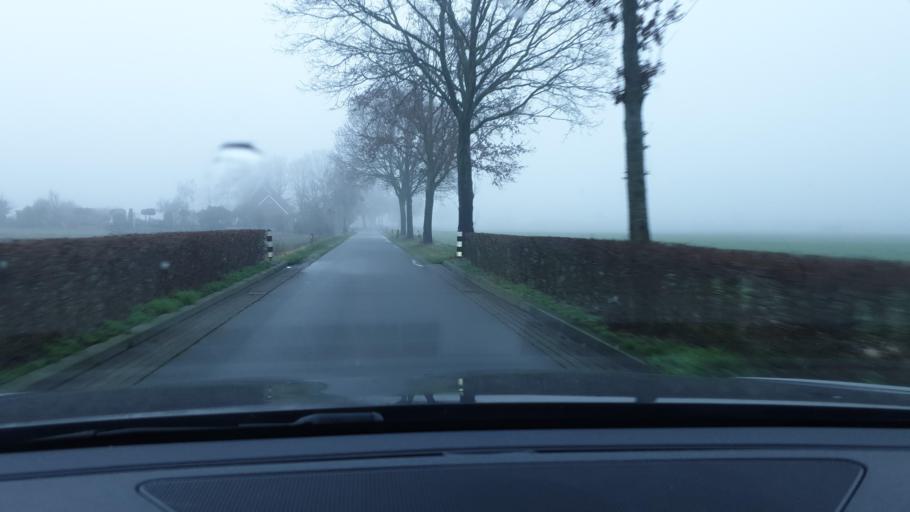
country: NL
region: North Brabant
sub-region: Gemeente Asten
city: Asten
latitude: 51.3875
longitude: 5.8659
